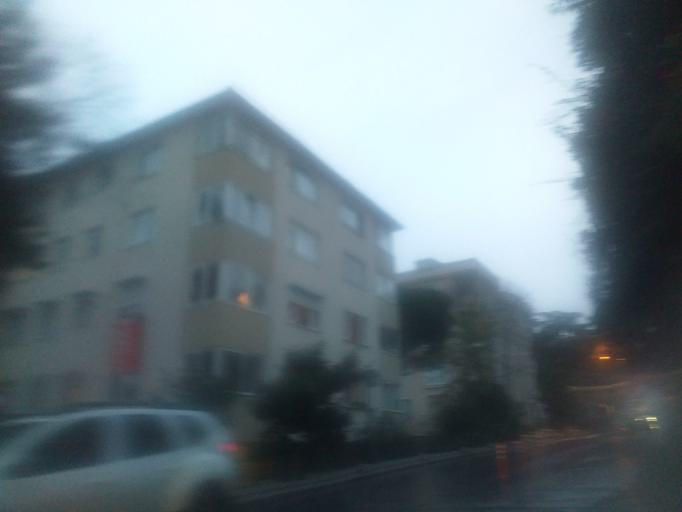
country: TR
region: Istanbul
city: UEskuedar
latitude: 41.0079
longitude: 29.0527
